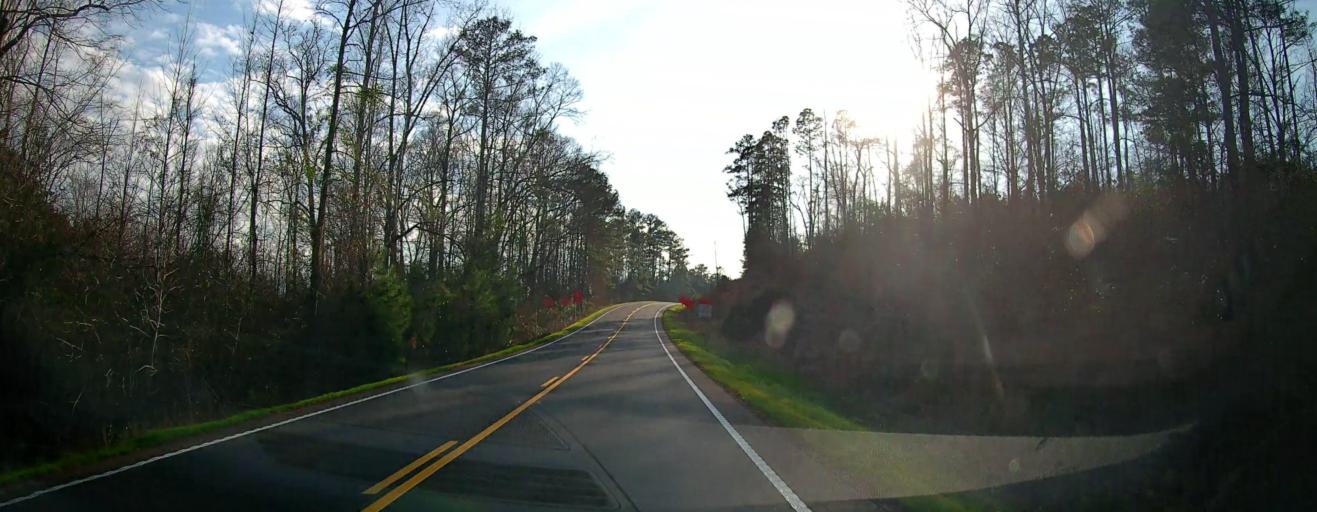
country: US
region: Georgia
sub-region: Harris County
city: Hamilton
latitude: 32.7498
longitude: -84.9085
